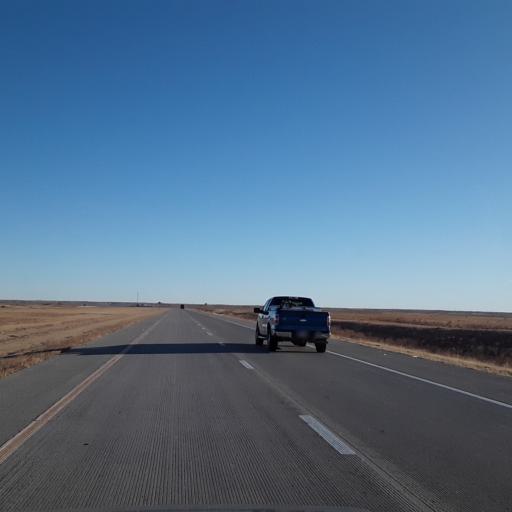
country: US
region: Kansas
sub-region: Seward County
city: Liberal
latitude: 37.1087
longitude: -100.7857
